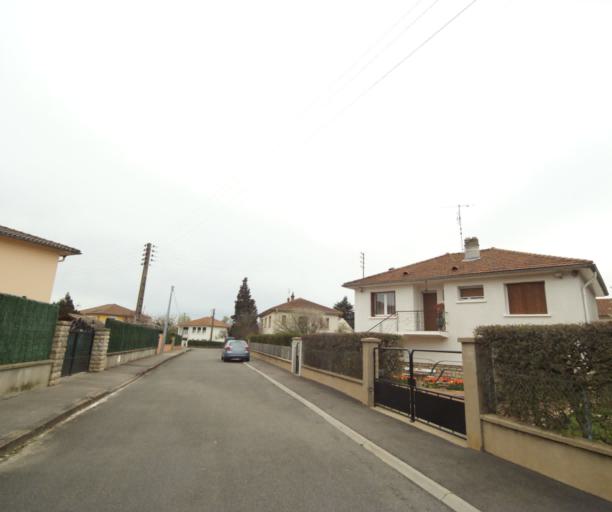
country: FR
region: Bourgogne
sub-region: Departement de Saone-et-Loire
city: Charnay-les-Macon
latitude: 46.3064
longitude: 4.8087
